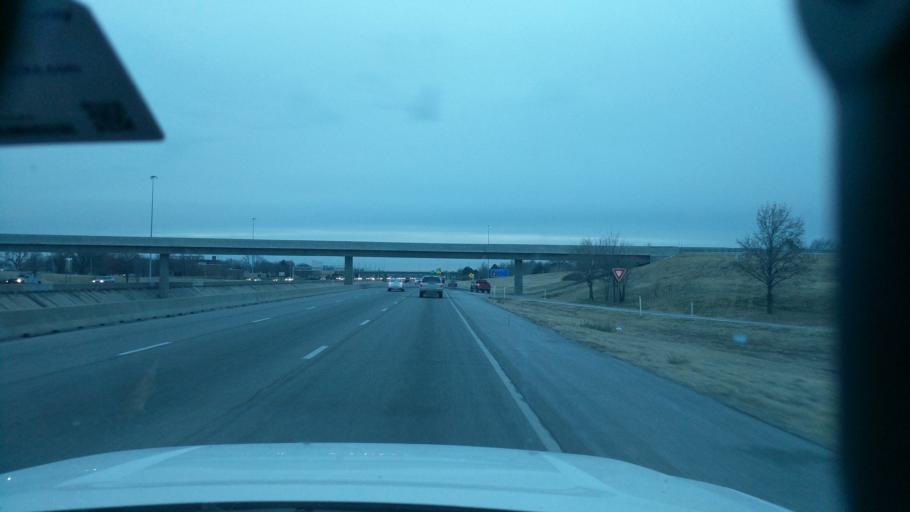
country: US
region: Kansas
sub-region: Sedgwick County
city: Wichita
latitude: 37.6773
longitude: -97.3129
